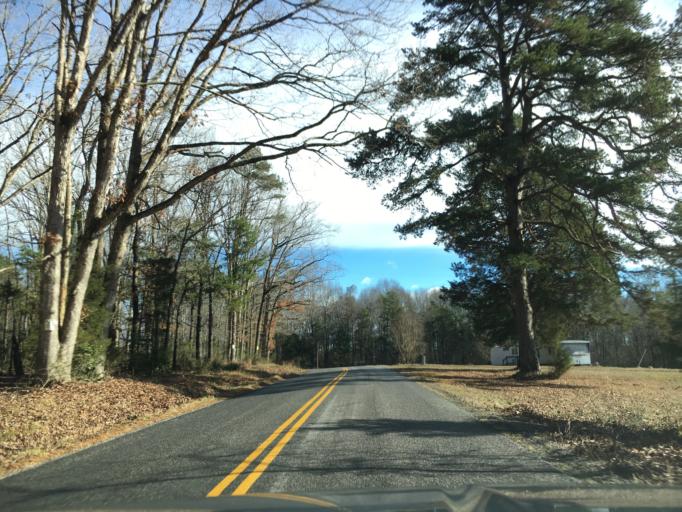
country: US
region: Virginia
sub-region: Amelia County
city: Amelia Court House
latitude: 37.4377
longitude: -78.0278
